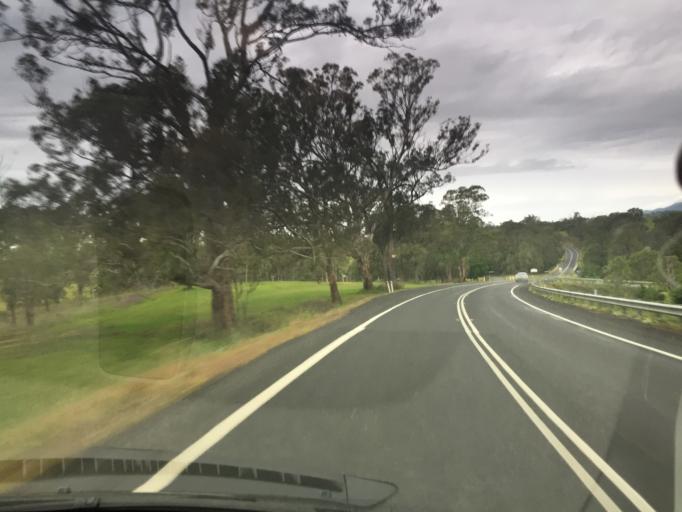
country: AU
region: New South Wales
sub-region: Bega Valley
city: Bega
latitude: -36.6330
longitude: 149.5767
